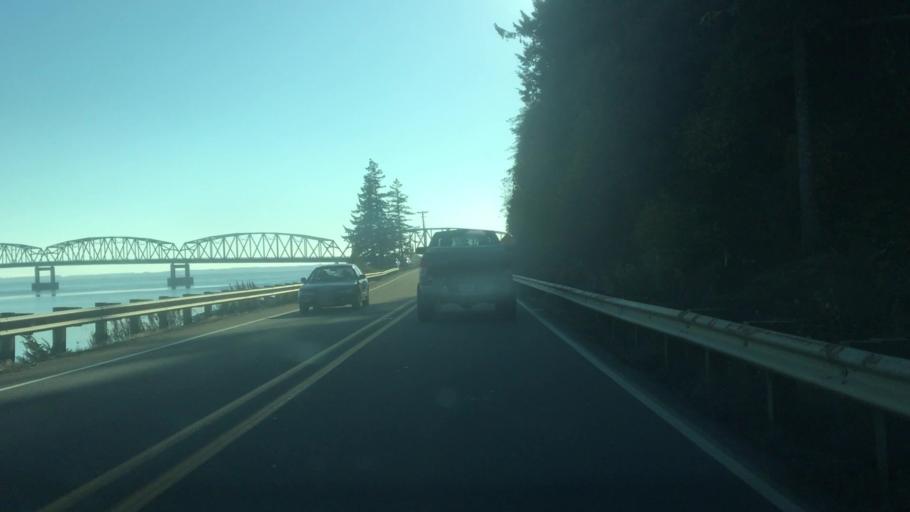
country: US
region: Oregon
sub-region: Clatsop County
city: Astoria
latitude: 46.2428
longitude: -123.8709
